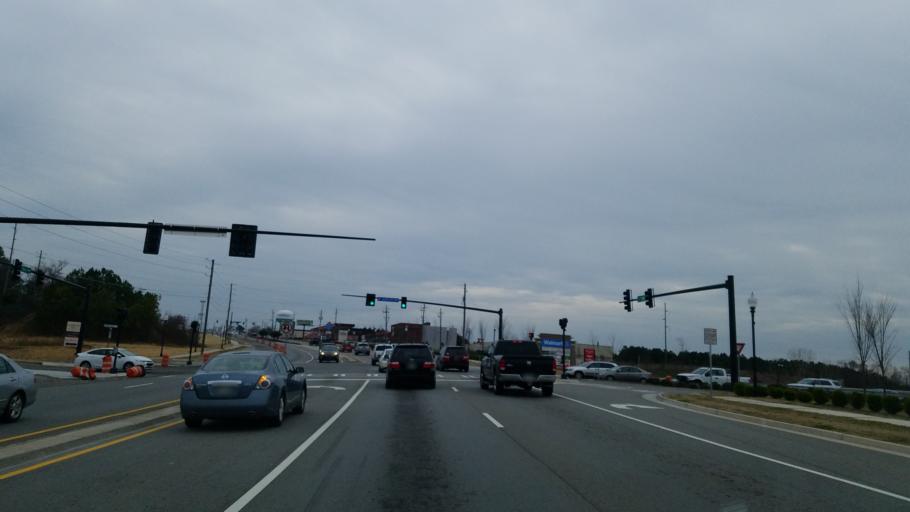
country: US
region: Georgia
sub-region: Cherokee County
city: Holly Springs
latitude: 34.1834
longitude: -84.5036
